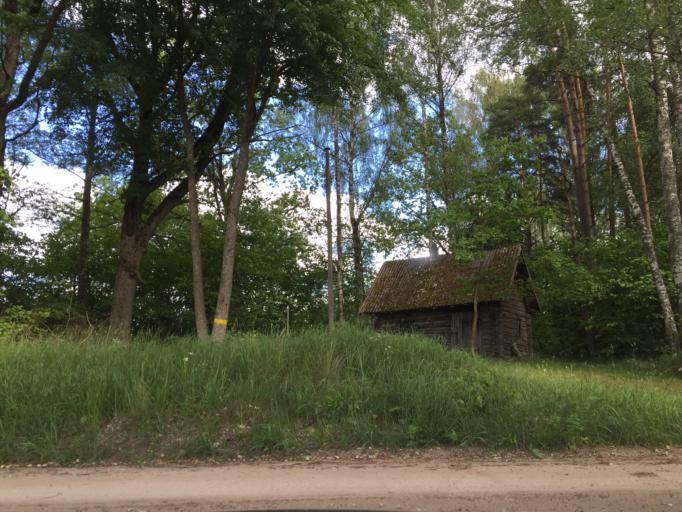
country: LV
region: Lecava
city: Iecava
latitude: 56.5612
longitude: 24.3123
